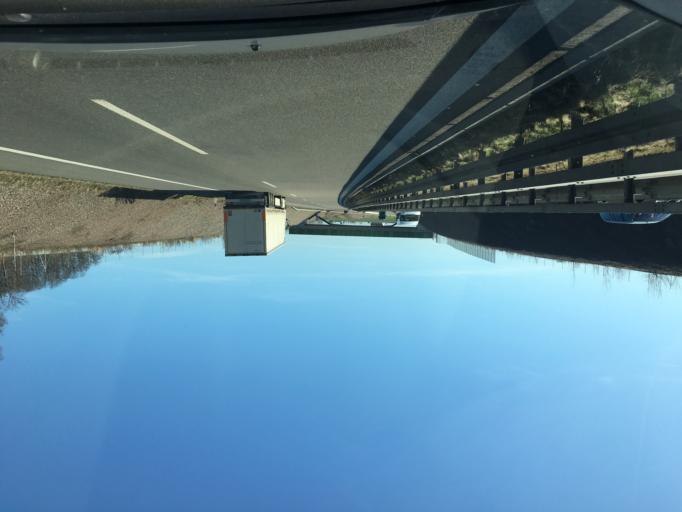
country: DE
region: Saxony
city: Narsdorf
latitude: 51.0184
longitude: 12.6833
